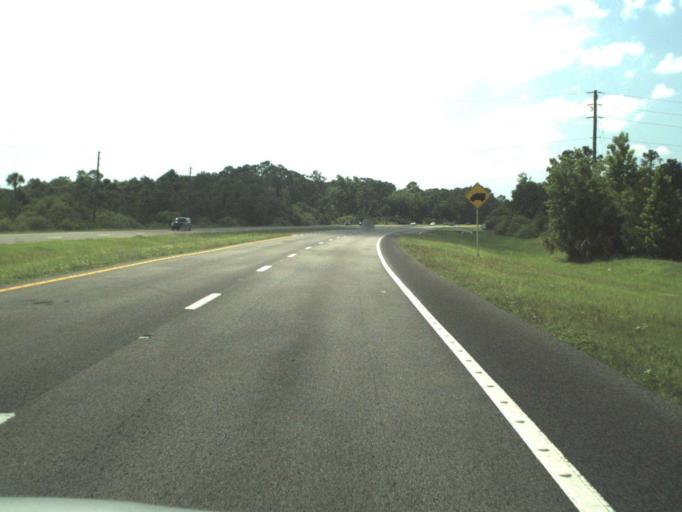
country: US
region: Florida
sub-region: Orange County
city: Christmas
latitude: 28.3896
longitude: -80.9375
